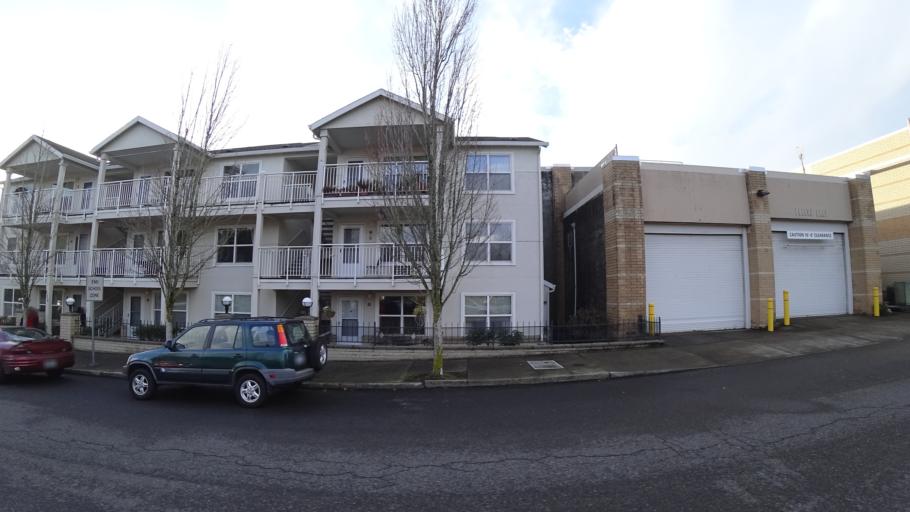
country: US
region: Oregon
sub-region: Multnomah County
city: Lents
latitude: 45.5168
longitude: -122.5539
